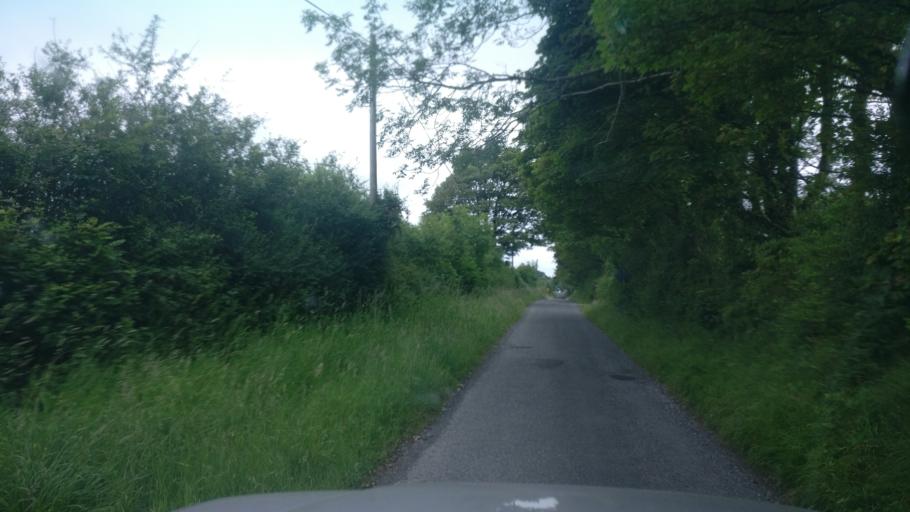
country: IE
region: Connaught
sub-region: County Galway
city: Ballinasloe
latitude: 53.3023
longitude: -8.3616
